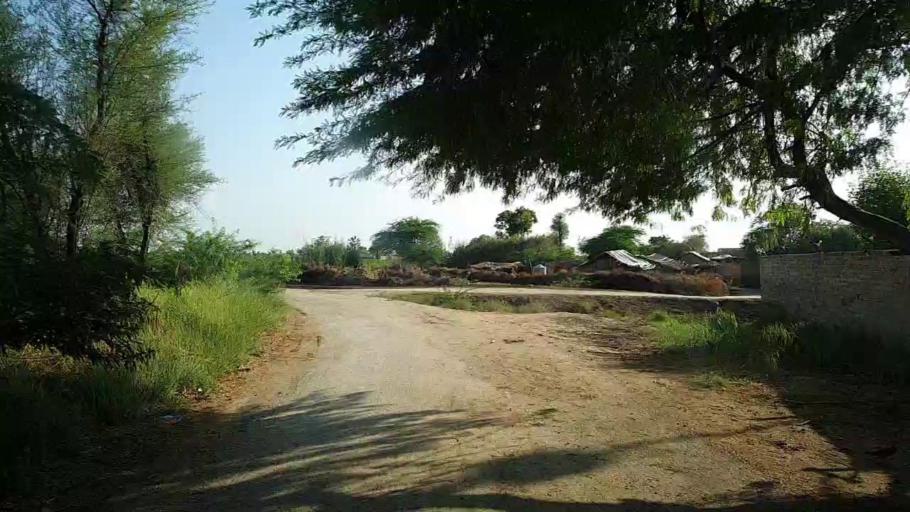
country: PK
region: Sindh
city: Hingorja
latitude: 27.0936
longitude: 68.3649
